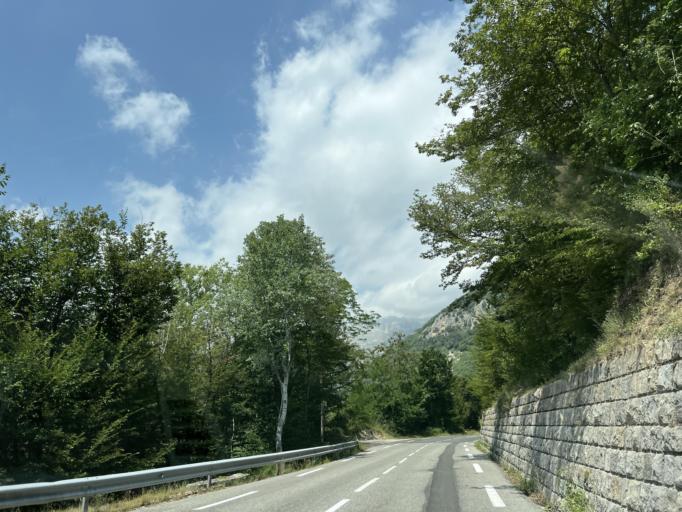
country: FR
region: Provence-Alpes-Cote d'Azur
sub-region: Departement des Alpes-Maritimes
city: Tourrettes-sur-Loup
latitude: 43.7689
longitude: 6.9850
